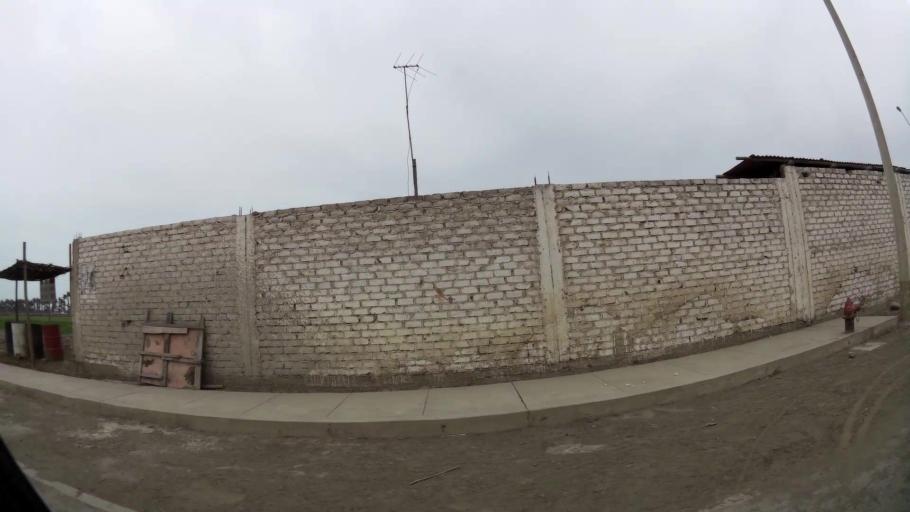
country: PE
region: Lima
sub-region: Barranca
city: Barranca
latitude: -10.7395
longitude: -77.7627
